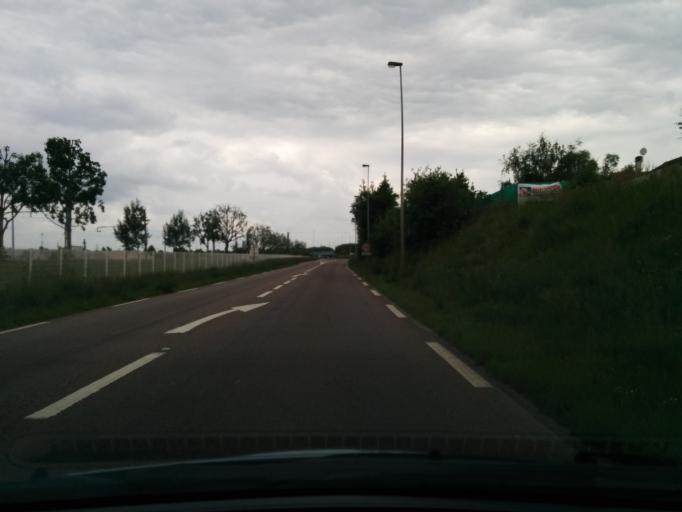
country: FR
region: Ile-de-France
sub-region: Departement des Yvelines
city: Limay
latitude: 48.9820
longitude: 1.7451
